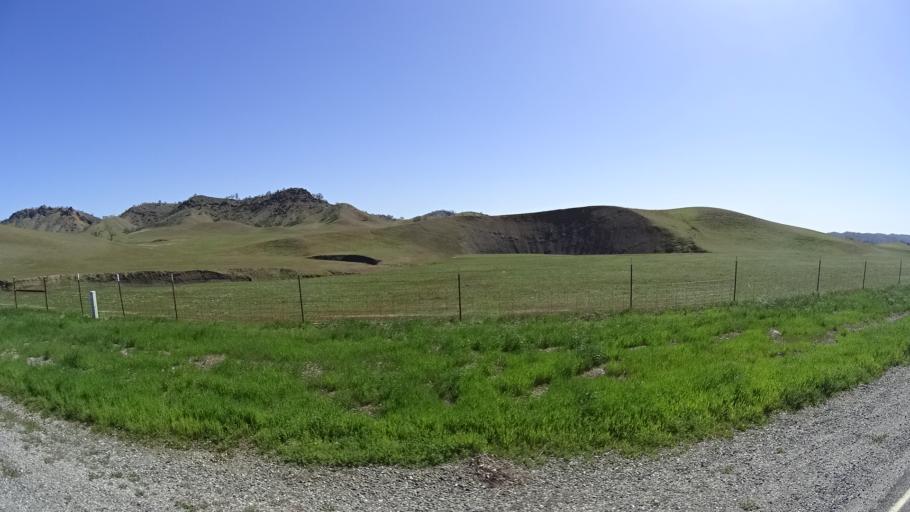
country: US
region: California
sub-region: Tehama County
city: Rancho Tehama Reserve
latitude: 39.7057
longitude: -122.5515
